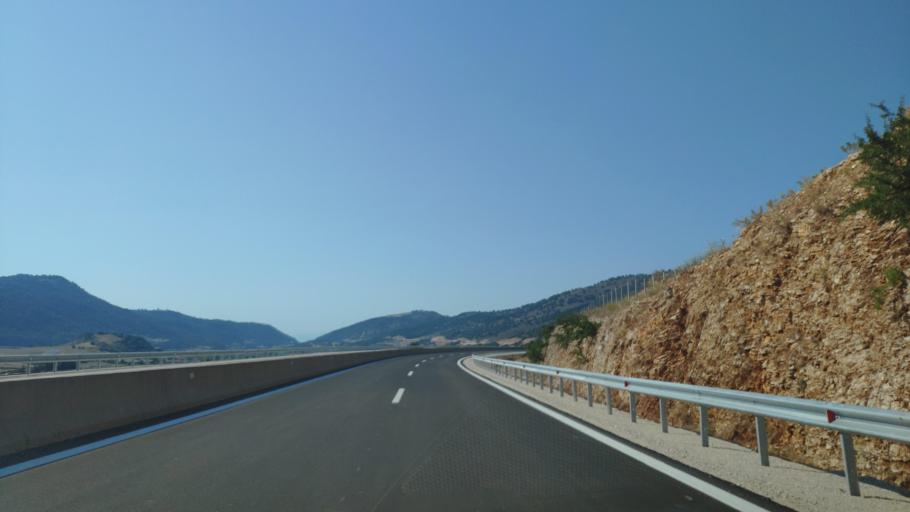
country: GR
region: West Greece
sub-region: Nomos Aitolias kai Akarnanias
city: Katouna
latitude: 38.8086
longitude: 21.1300
